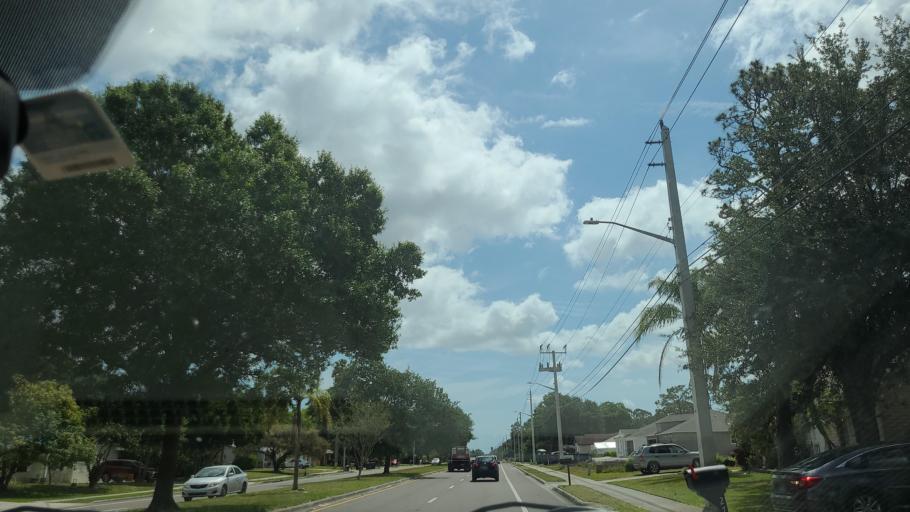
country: US
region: Florida
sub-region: Brevard County
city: June Park
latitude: 28.0318
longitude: -80.6907
